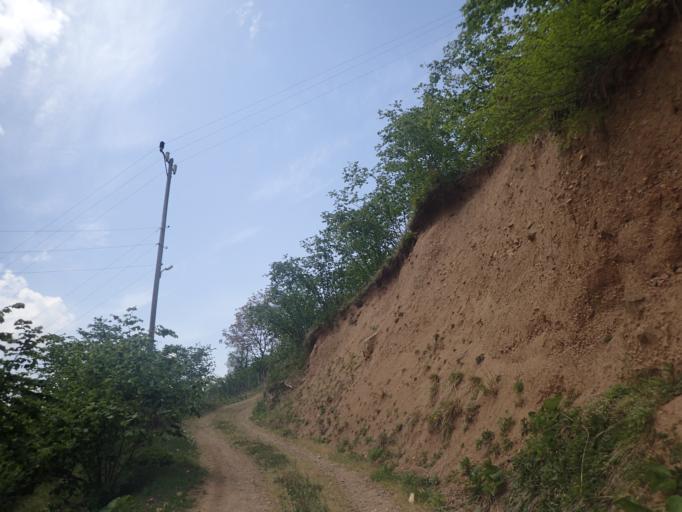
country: TR
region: Ordu
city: Kabaduz
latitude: 40.7975
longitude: 37.8886
